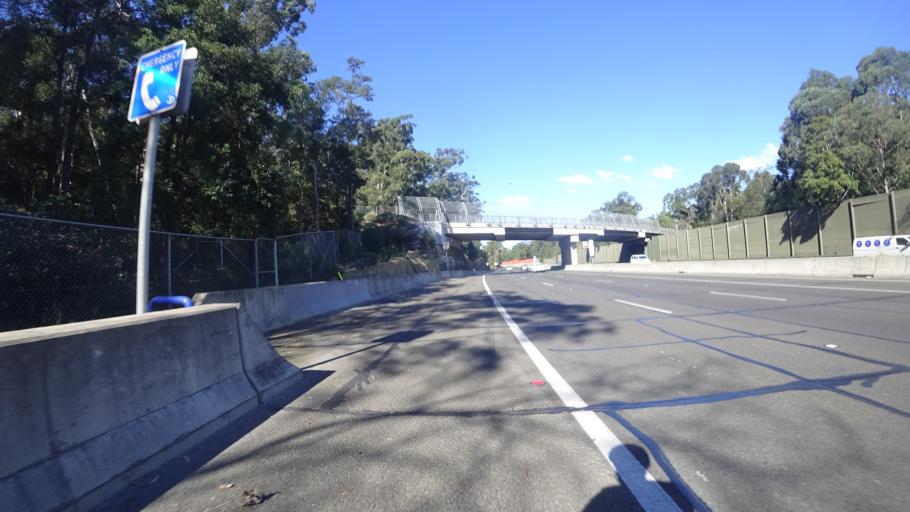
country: AU
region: New South Wales
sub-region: Hornsby Shire
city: Beecroft
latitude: -33.7582
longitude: 151.0654
